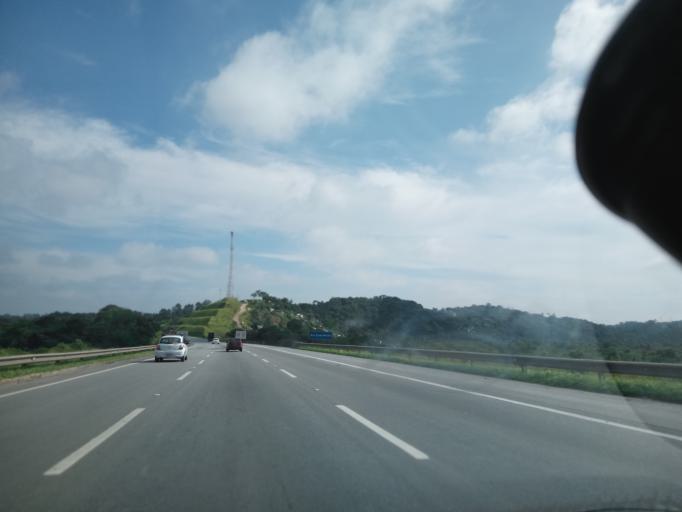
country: BR
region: Sao Paulo
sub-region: Itapecerica Da Serra
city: Itapecerica da Serra
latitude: -23.7222
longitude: -46.8061
